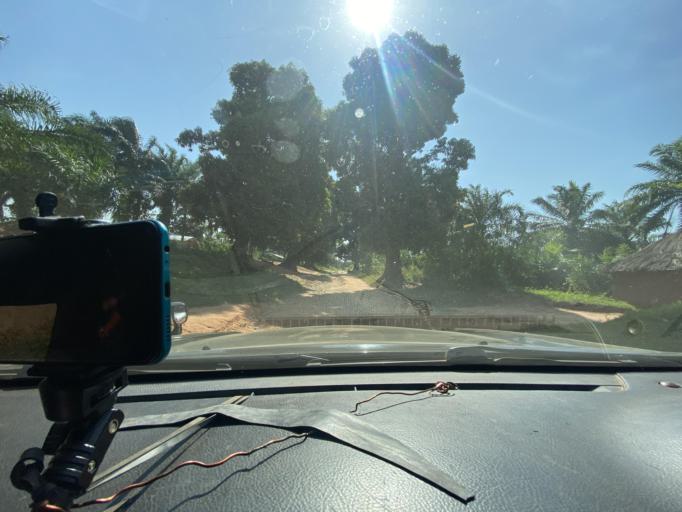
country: CD
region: Kasai-Oriental
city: Kabinda
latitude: -6.1111
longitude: 24.5309
